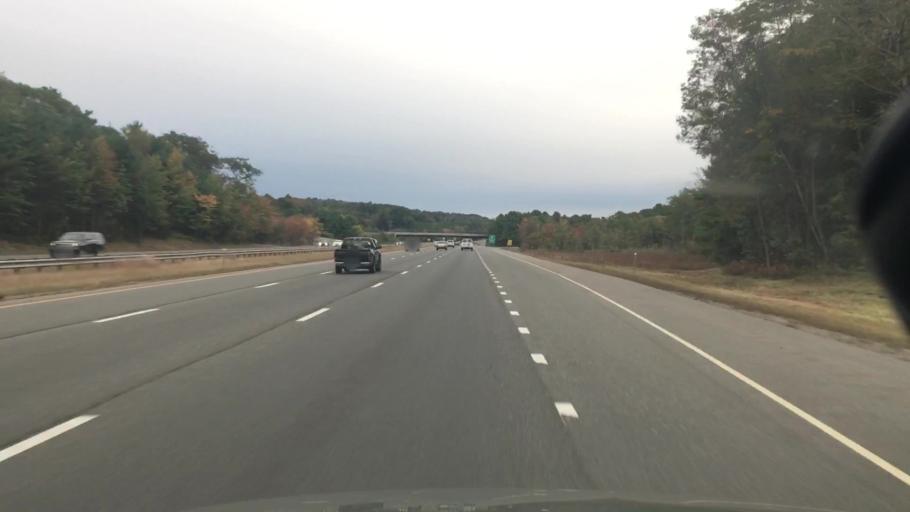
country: US
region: Massachusetts
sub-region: Hampden County
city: Holland
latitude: 41.9805
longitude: -72.1801
